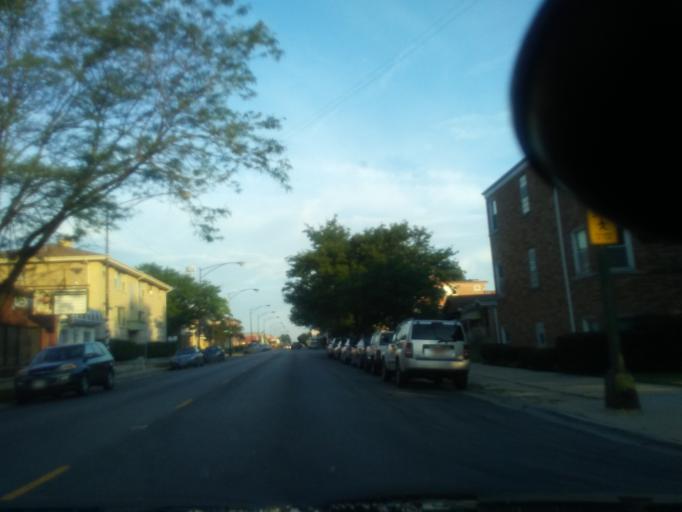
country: US
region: Illinois
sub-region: Cook County
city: Harwood Heights
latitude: 41.9796
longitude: -87.8001
